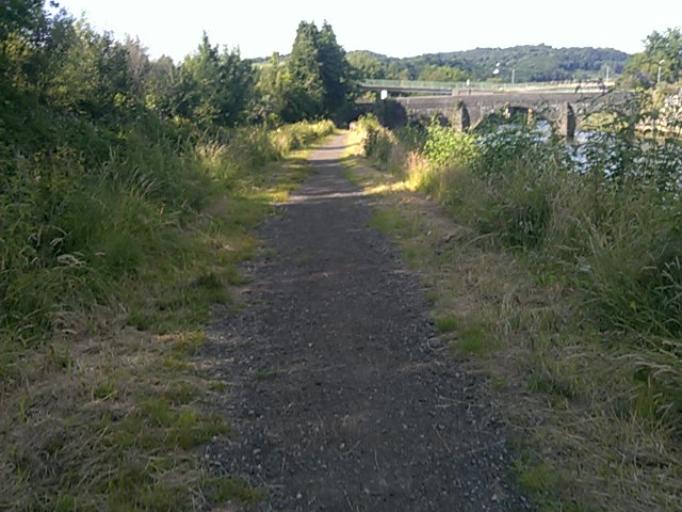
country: GB
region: Wales
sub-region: Neath Port Talbot
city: Neath
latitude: 51.6641
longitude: -3.8099
